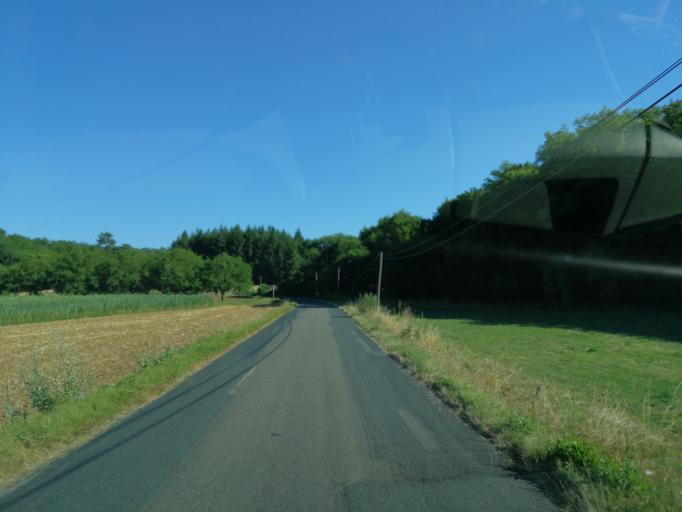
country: FR
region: Midi-Pyrenees
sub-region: Departement du Lot
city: Gourdon
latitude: 44.7835
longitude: 1.3633
